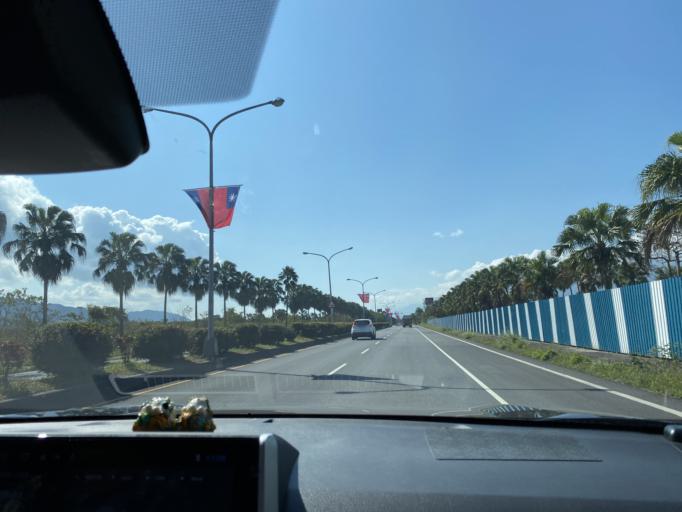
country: TW
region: Taiwan
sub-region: Hualien
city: Hualian
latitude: 23.8656
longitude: 121.5318
